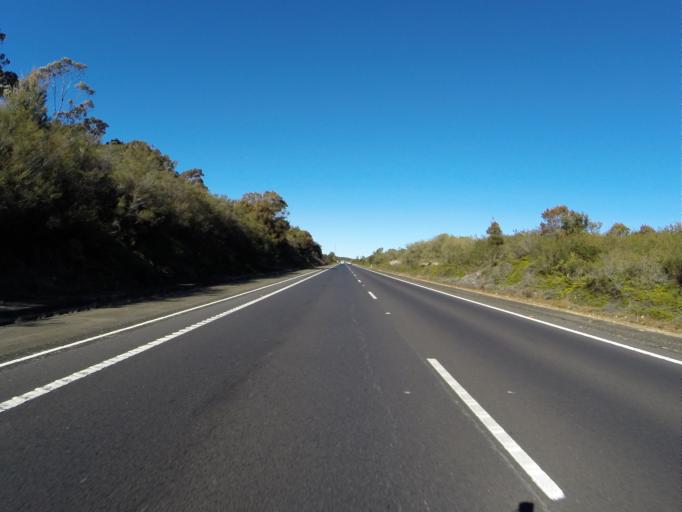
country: AU
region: New South Wales
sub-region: Wollongong
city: Bulli
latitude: -34.2717
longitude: 150.9271
